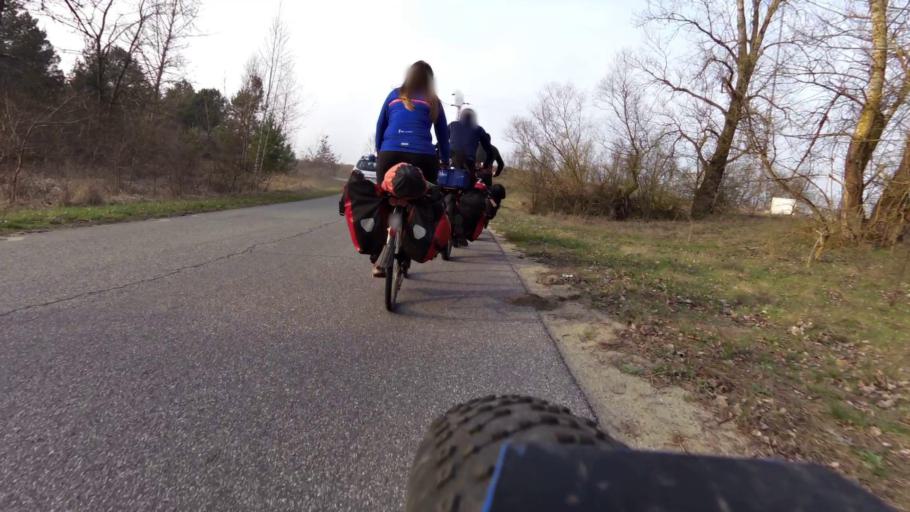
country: DE
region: Brandenburg
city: Vogelsang
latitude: 52.2528
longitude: 14.7043
